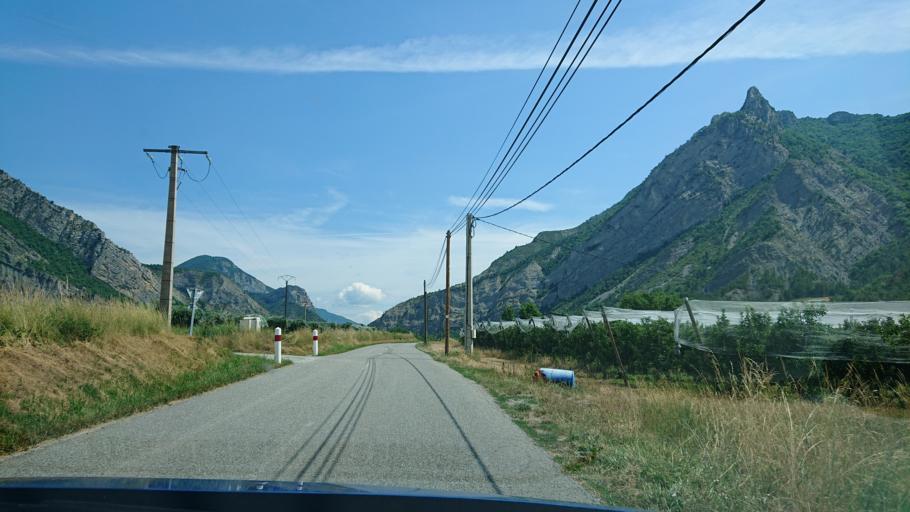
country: FR
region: Provence-Alpes-Cote d'Azur
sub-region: Departement des Hautes-Alpes
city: Tallard
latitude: 44.3540
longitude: 6.0424
